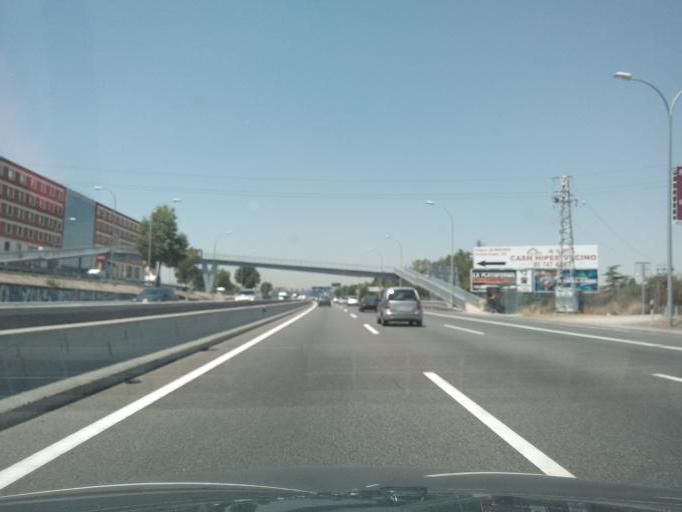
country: ES
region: Madrid
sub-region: Provincia de Madrid
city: Coslada
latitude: 40.4495
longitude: -3.5570
